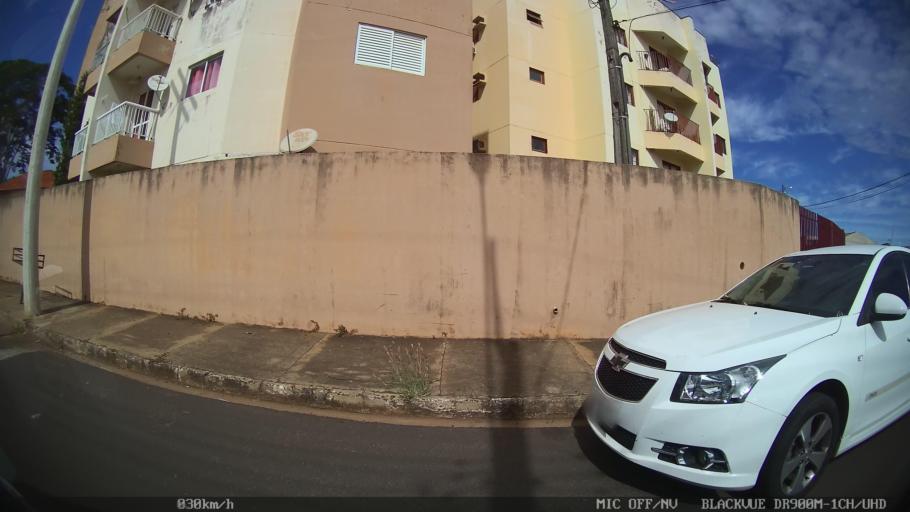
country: BR
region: Sao Paulo
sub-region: Bady Bassitt
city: Bady Bassitt
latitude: -20.8132
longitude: -49.5164
